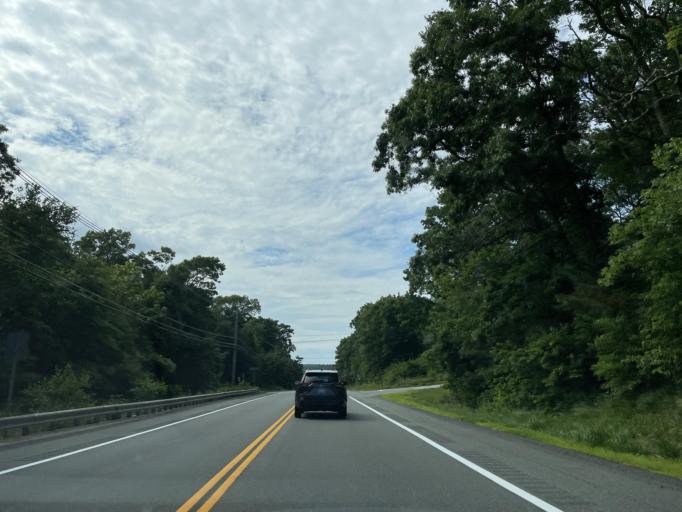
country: US
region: Rhode Island
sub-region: Kent County
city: West Greenwich
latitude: 41.6198
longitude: -71.6737
